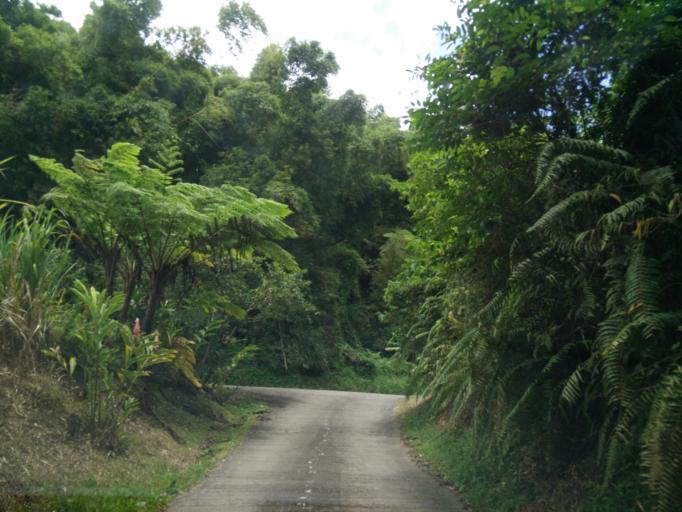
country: MQ
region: Martinique
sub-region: Martinique
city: Le Morne-Rouge
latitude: 14.7842
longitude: -61.1431
